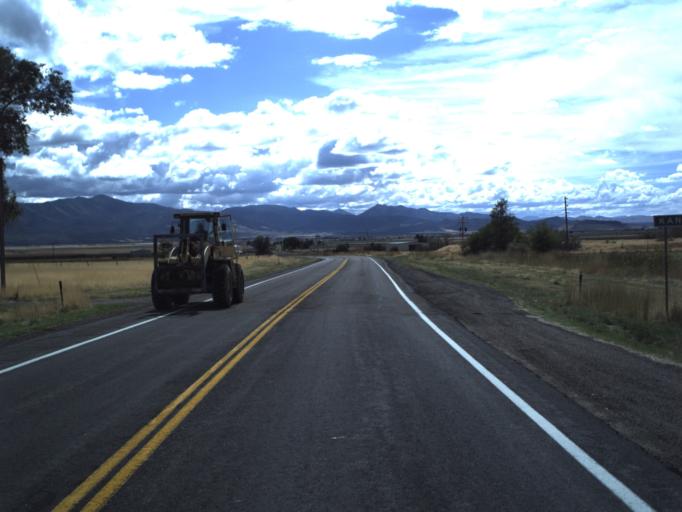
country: US
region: Utah
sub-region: Millard County
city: Fillmore
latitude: 38.8810
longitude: -112.4110
